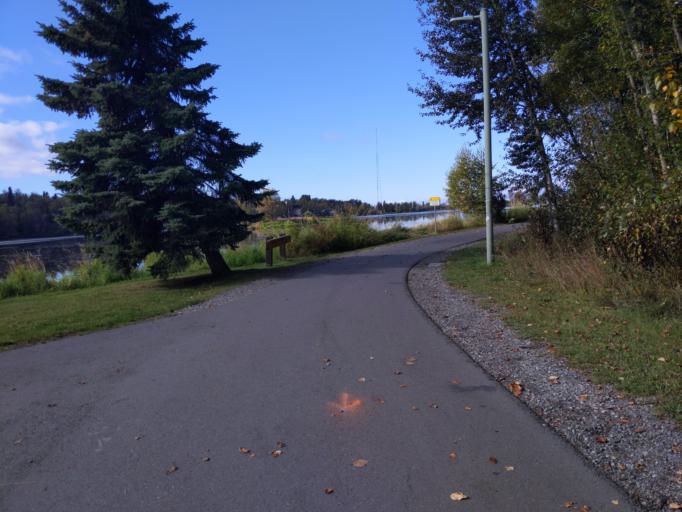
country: US
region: Alaska
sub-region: Anchorage Municipality
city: Anchorage
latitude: 61.2059
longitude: -149.9128
